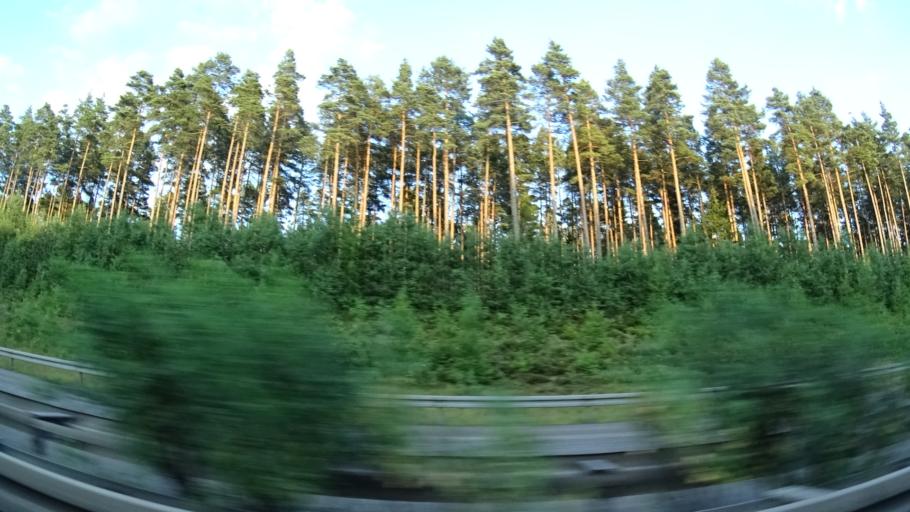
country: DE
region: Thuringia
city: Behringen
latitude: 50.7302
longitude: 10.9831
